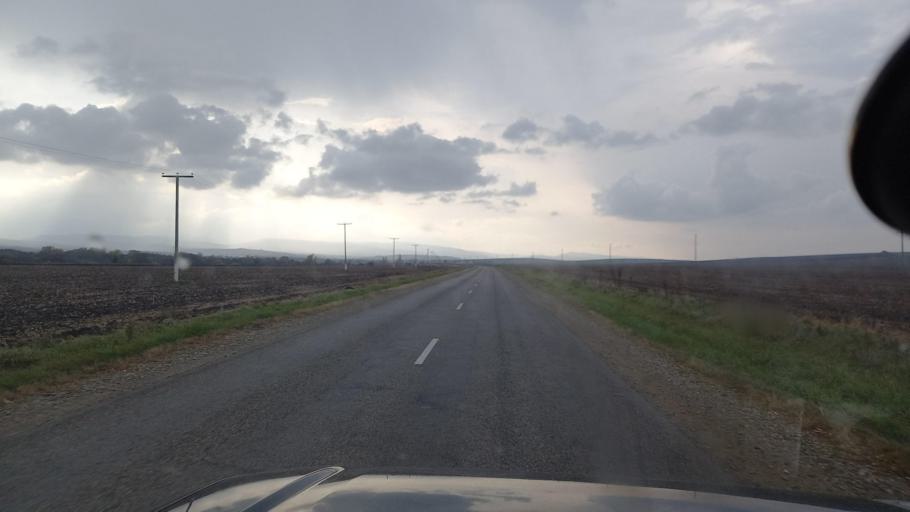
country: RU
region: Krasnodarskiy
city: Gubskaya
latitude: 44.3493
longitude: 40.6926
